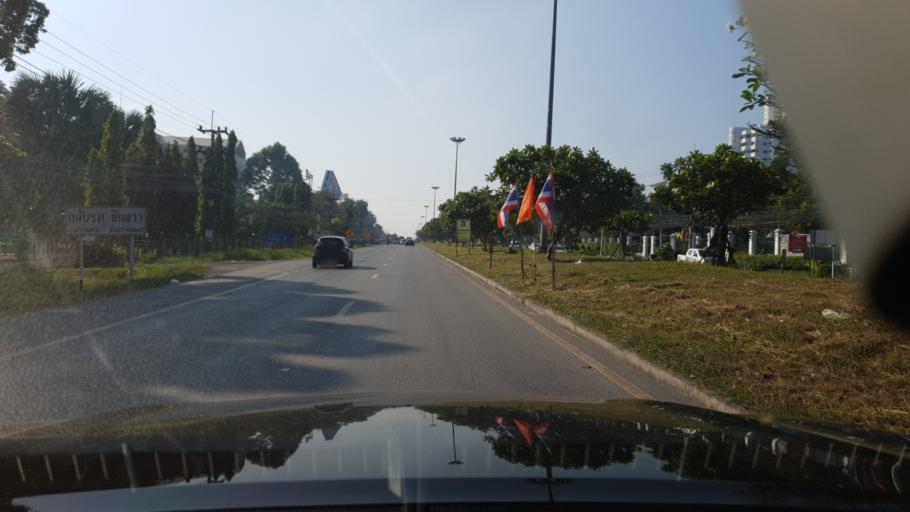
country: TH
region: Chon Buri
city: Phatthaya
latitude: 12.8118
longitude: 100.9169
